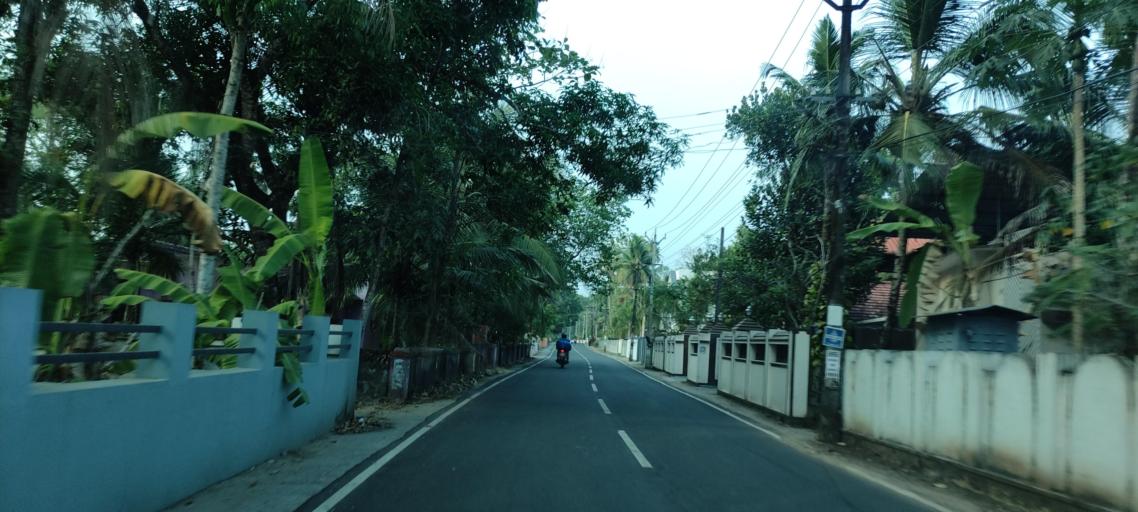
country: IN
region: Kerala
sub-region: Alappuzha
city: Mavelikara
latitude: 9.2638
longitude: 76.5562
